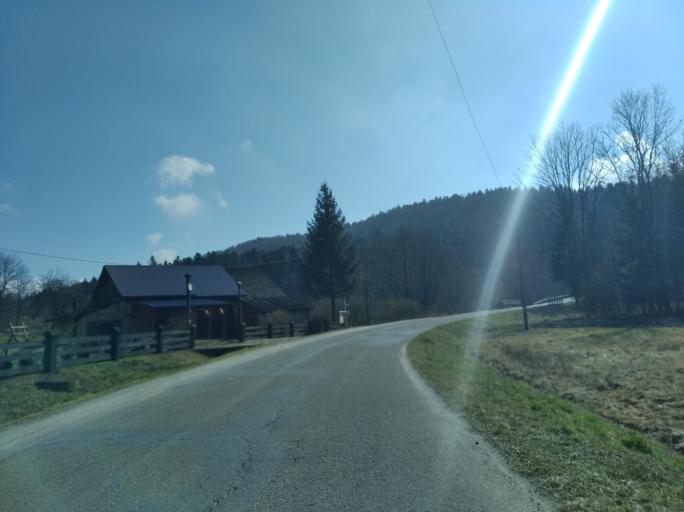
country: PL
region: Subcarpathian Voivodeship
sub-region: Powiat strzyzowski
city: Frysztak
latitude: 49.8679
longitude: 21.5597
